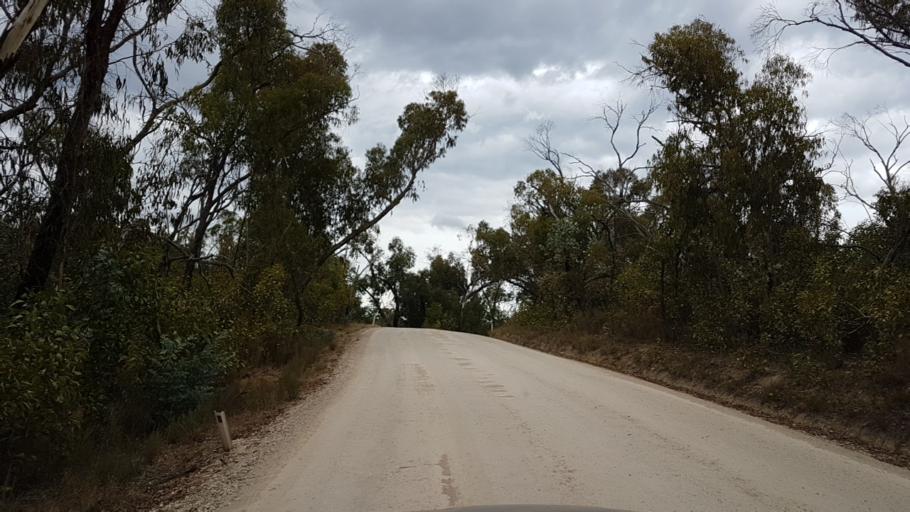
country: AU
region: South Australia
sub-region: Adelaide Hills
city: Gumeracha
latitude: -34.7943
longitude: 138.8343
